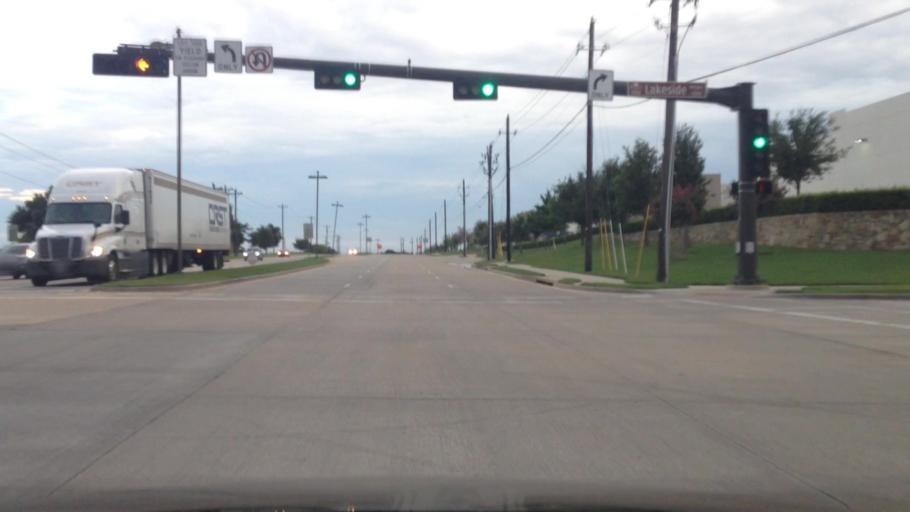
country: US
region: Texas
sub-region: Dallas County
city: Coppell
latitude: 32.9949
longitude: -97.0457
